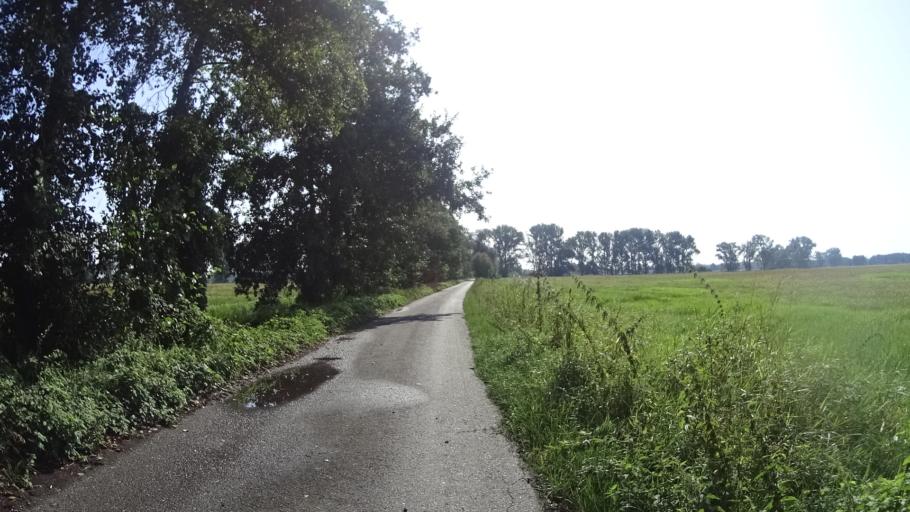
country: DE
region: Brandenburg
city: Neu Zauche
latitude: 51.9035
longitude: 14.0813
